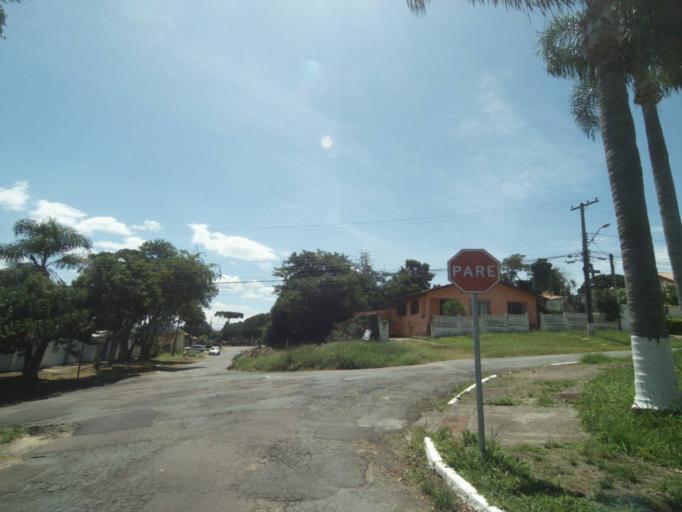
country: BR
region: Parana
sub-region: Curitiba
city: Curitiba
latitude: -25.4672
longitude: -49.2459
